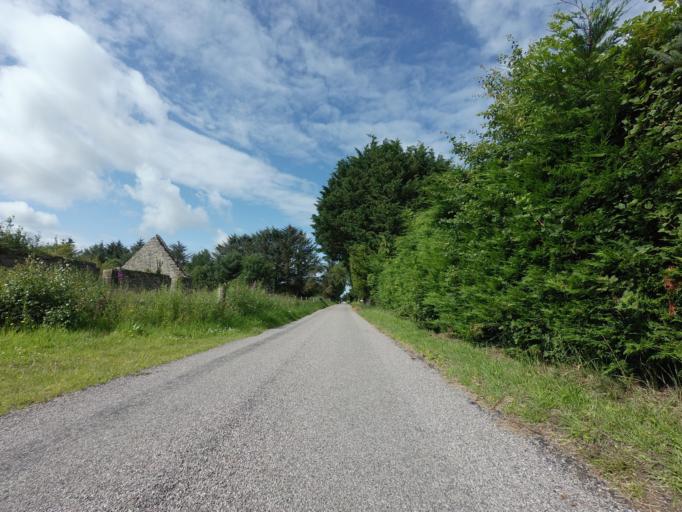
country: GB
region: Scotland
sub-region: Moray
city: Burghead
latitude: 57.6540
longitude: -3.4800
